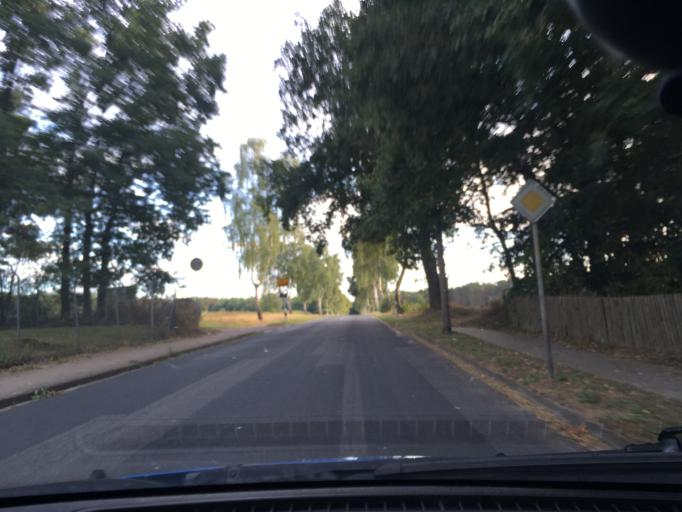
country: DE
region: Lower Saxony
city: Hanstedt
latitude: 53.2493
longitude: 10.0091
